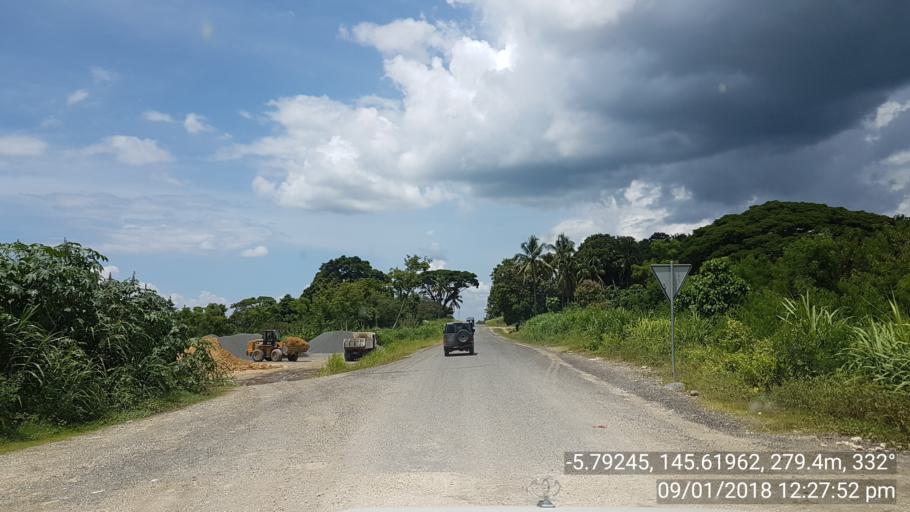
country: PG
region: Eastern Highlands
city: Goroka
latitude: -5.7924
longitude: 145.6196
